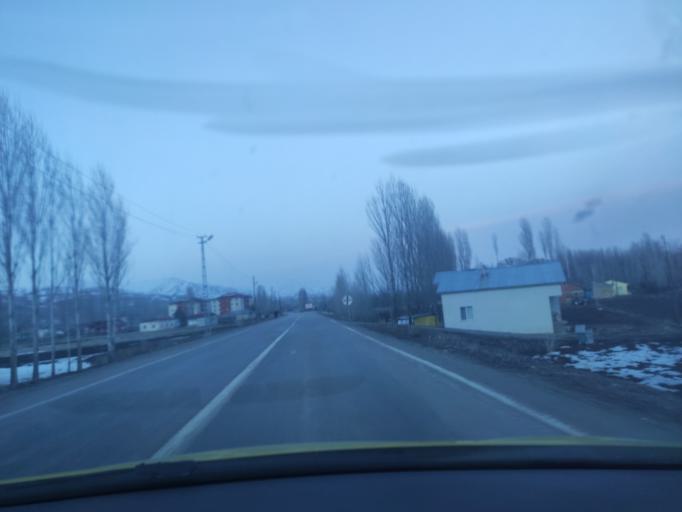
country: TR
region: Bayburt
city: Aydintepe
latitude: 40.3612
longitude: 40.1031
